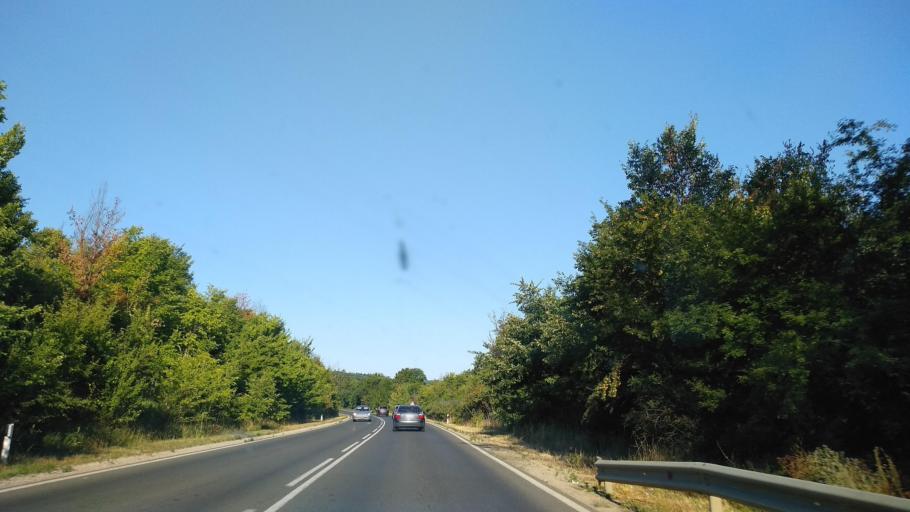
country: BG
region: Veliko Turnovo
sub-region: Obshtina Pavlikeni
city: Byala Cherkva
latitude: 43.0667
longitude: 25.2995
